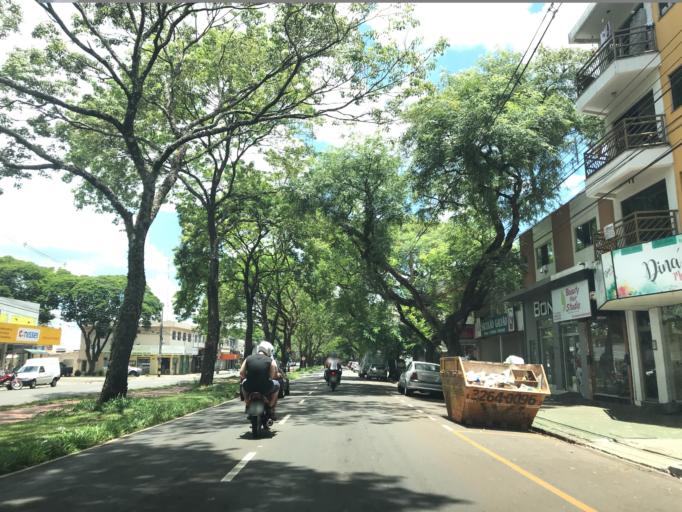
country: BR
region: Parana
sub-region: Maringa
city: Maringa
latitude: -23.4043
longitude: -51.9218
